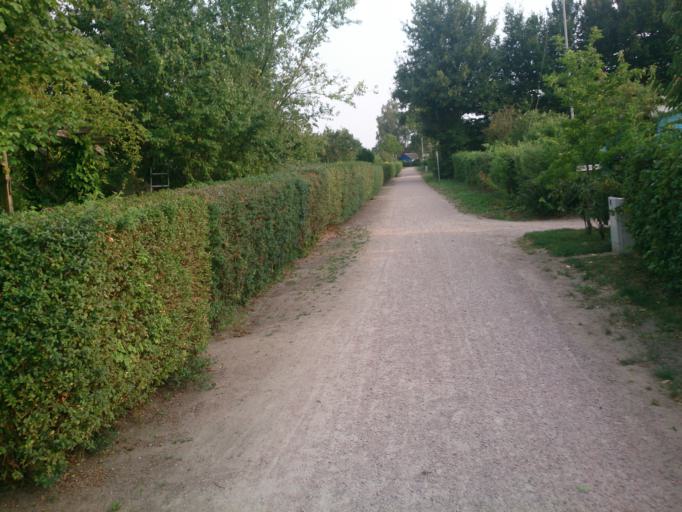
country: DE
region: Lower Saxony
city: Neu Wulmstorf
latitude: 53.5303
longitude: 9.8448
